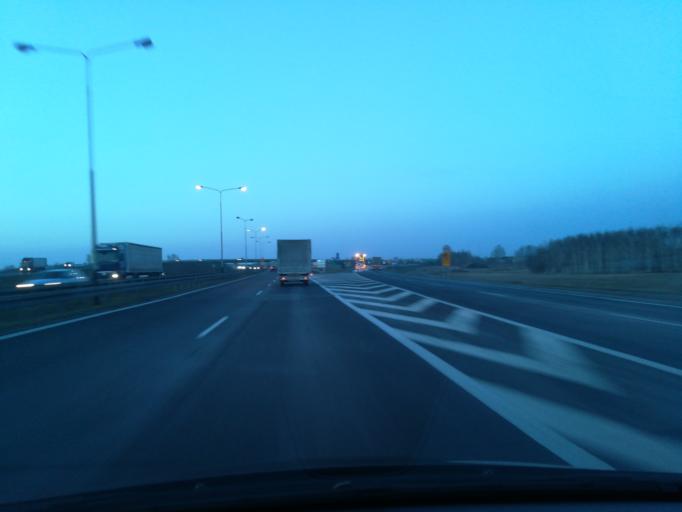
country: PL
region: Lodz Voivodeship
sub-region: Piotrkow Trybunalski
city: Piotrkow Trybunalski
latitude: 51.4323
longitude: 19.6419
